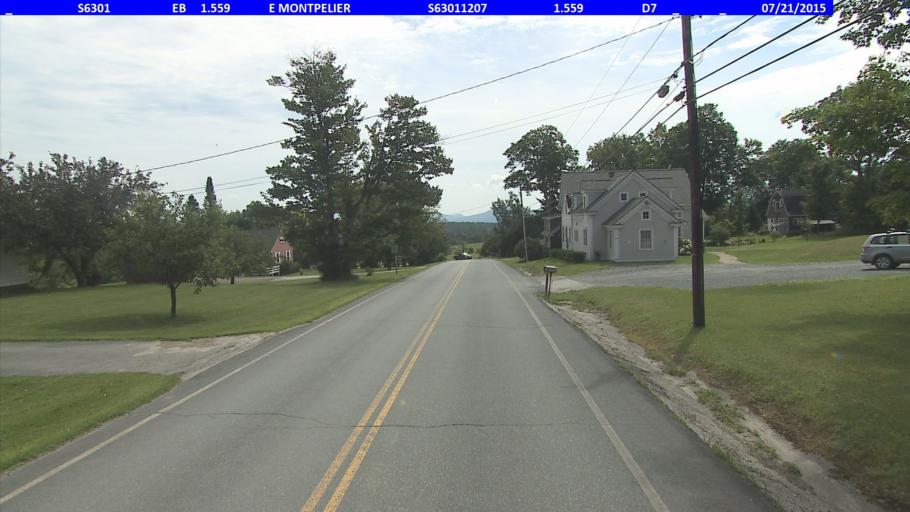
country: US
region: Vermont
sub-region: Washington County
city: Montpelier
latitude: 44.2835
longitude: -72.5269
